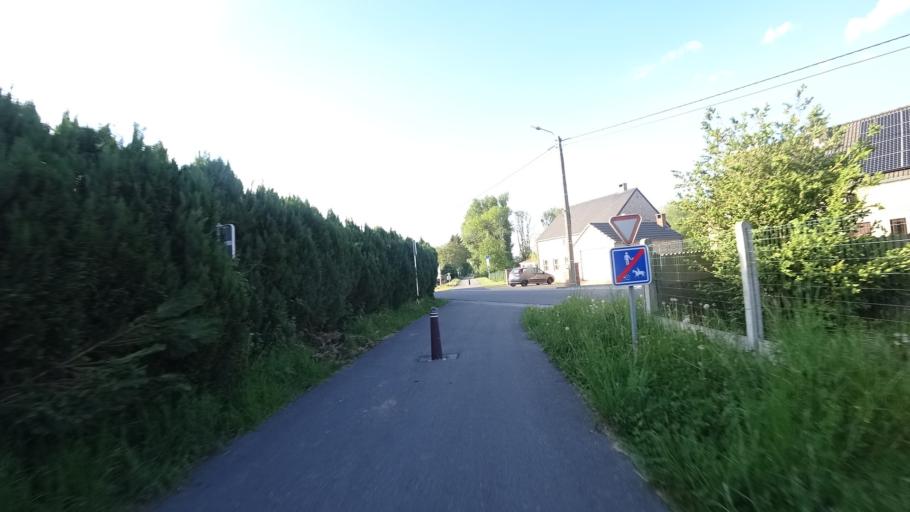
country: BE
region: Wallonia
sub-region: Province de Namur
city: Eghezee
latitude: 50.5520
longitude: 4.9038
